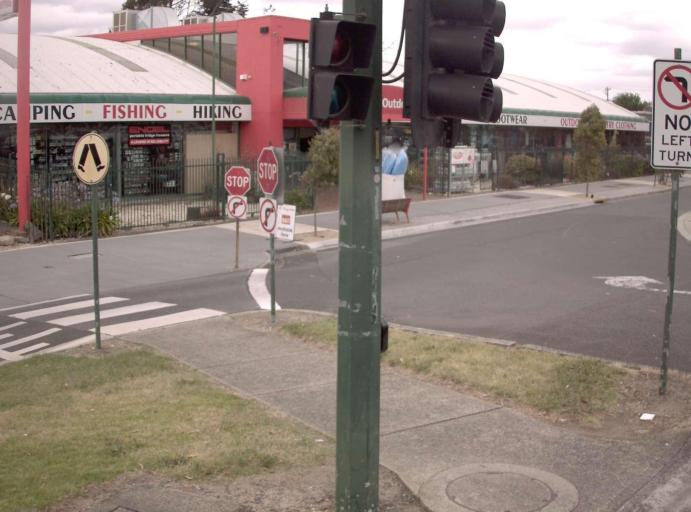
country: AU
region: Victoria
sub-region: Whitehorse
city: Nunawading
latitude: -37.8182
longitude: 145.1683
